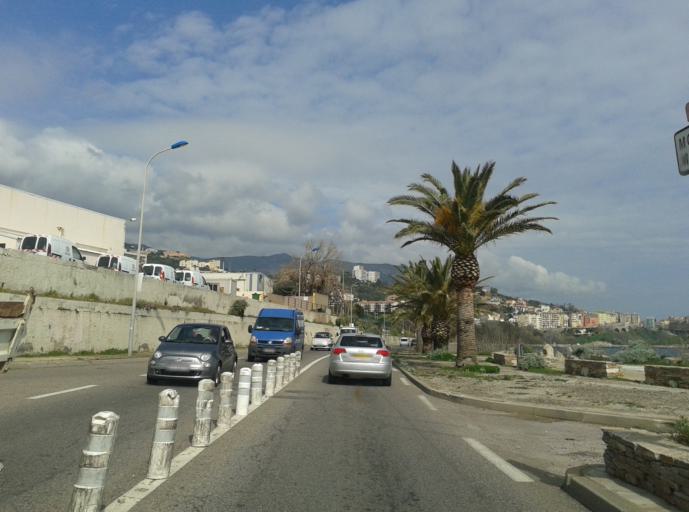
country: FR
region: Corsica
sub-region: Departement de la Haute-Corse
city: Bastia
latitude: 42.6805
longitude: 9.4470
